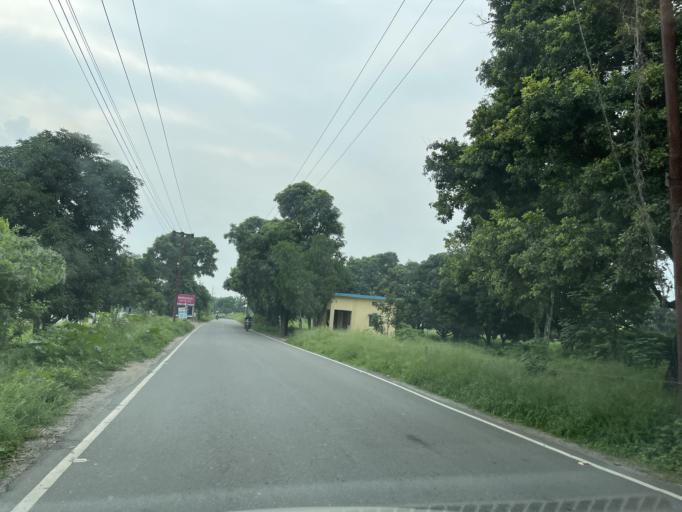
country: IN
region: Uttarakhand
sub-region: Naini Tal
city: Haldwani
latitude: 29.1735
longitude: 79.4791
